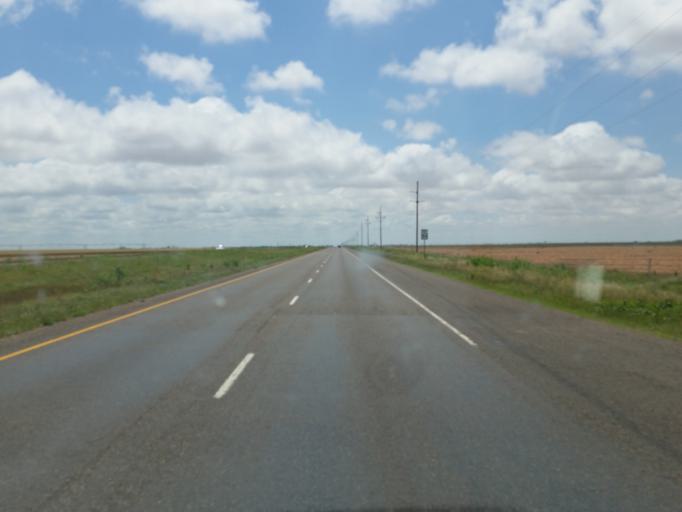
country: US
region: Texas
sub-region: Lubbock County
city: Slaton
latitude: 33.3917
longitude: -101.6012
